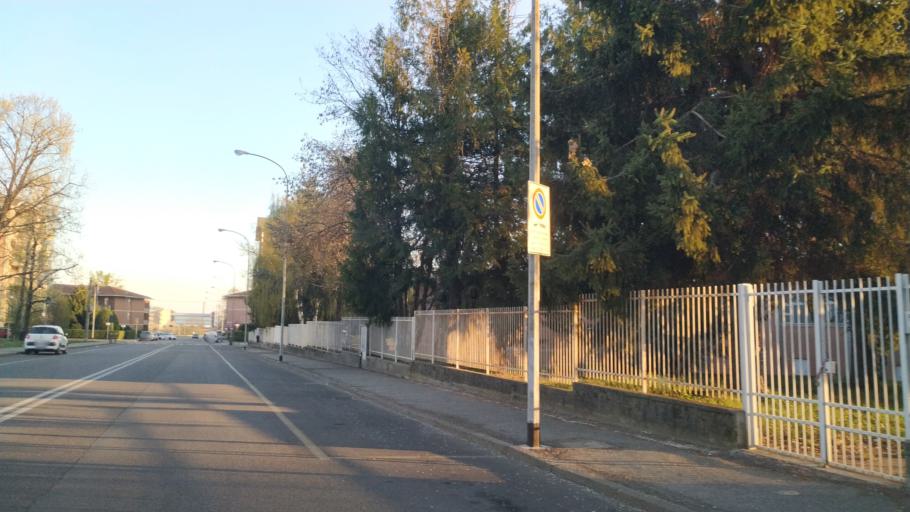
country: IT
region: Piedmont
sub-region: Provincia di Biella
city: Ponderano
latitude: 45.5502
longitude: 8.0584
